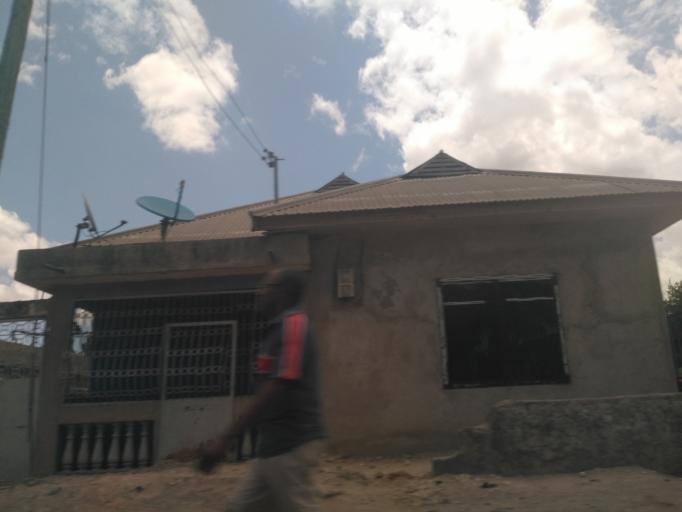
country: TZ
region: Dar es Salaam
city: Dar es Salaam
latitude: -6.8702
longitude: 39.2410
